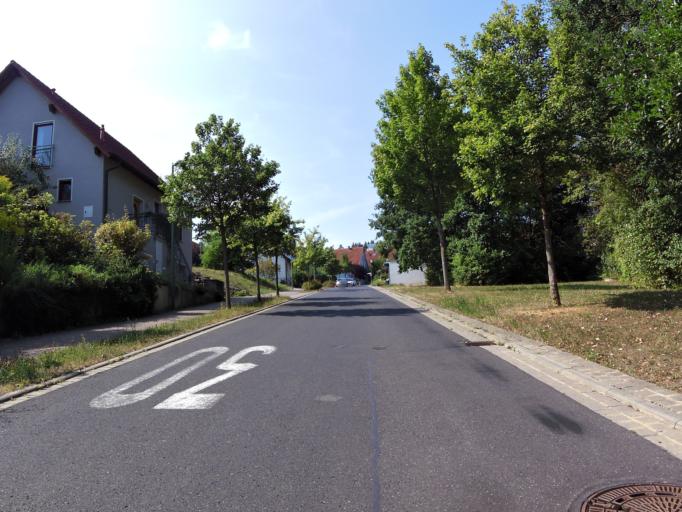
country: DE
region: Bavaria
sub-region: Regierungsbezirk Unterfranken
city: Zell am Main
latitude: 49.8132
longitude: 9.8662
